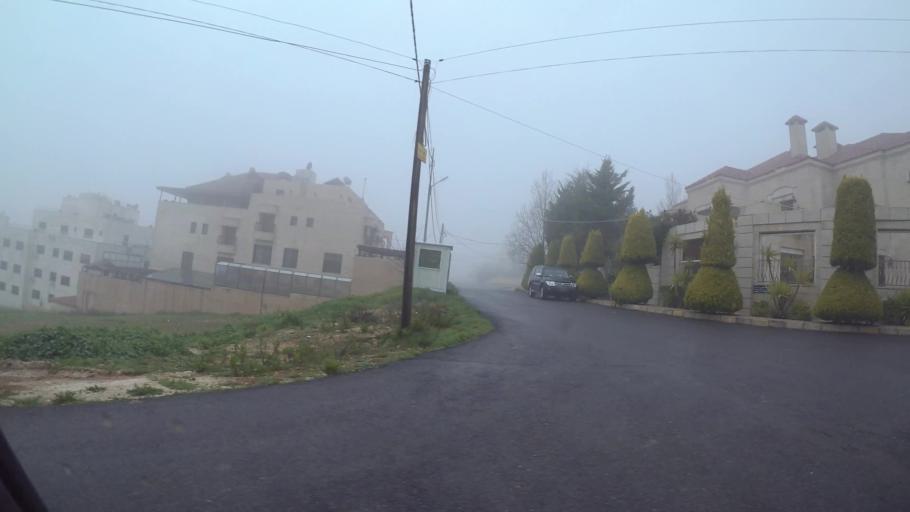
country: JO
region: Amman
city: Al Jubayhah
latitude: 32.0133
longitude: 35.8378
